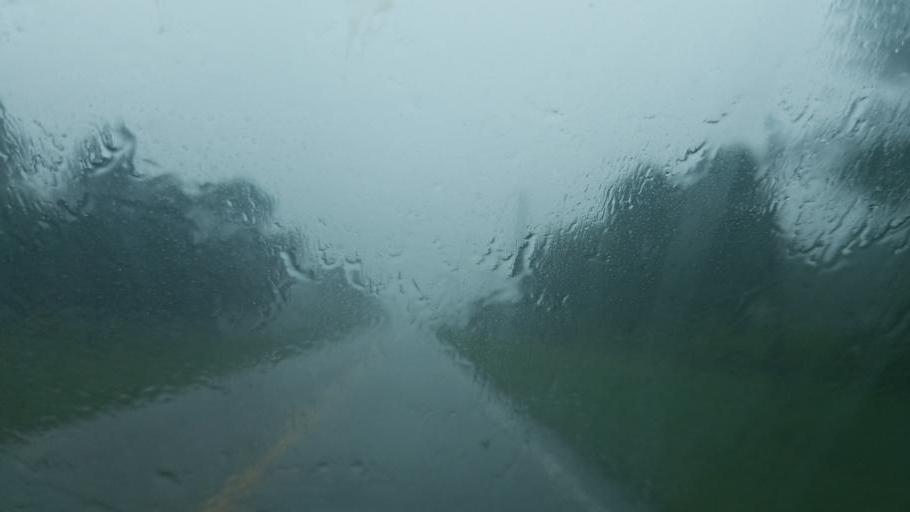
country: US
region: Kentucky
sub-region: Rowan County
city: Morehead
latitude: 38.2829
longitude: -83.5659
